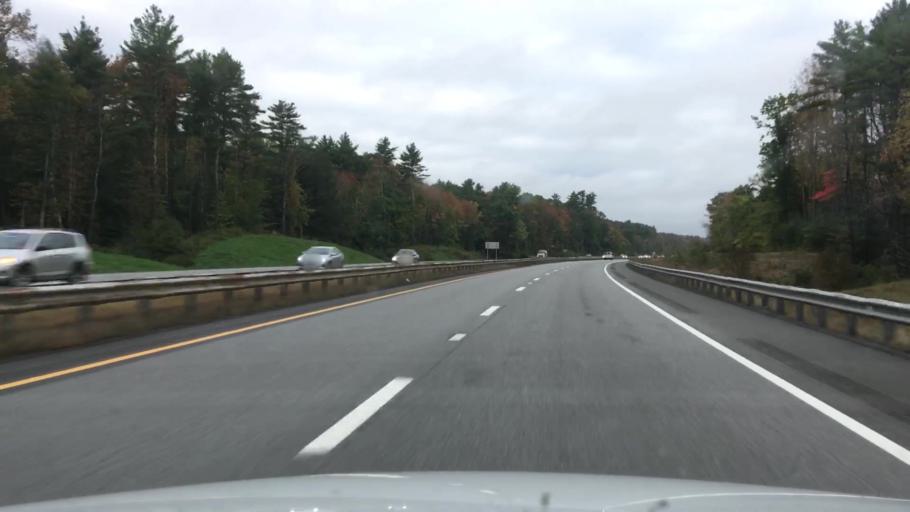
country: US
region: Maine
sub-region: Cumberland County
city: Cumberland Center
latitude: 43.7653
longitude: -70.3116
